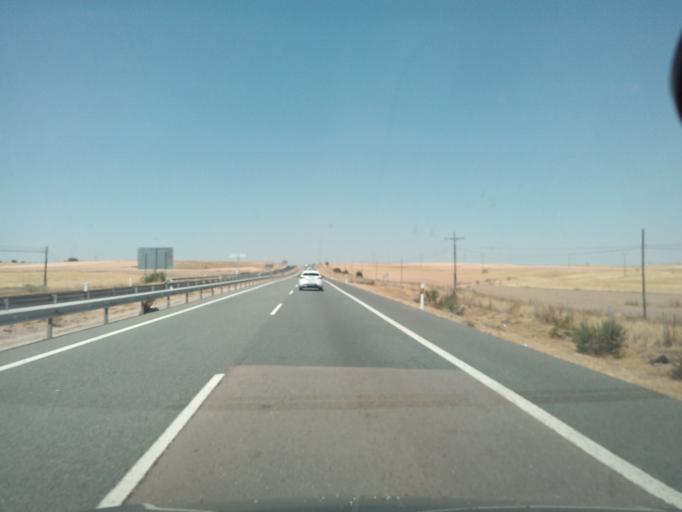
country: ES
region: Castille-La Mancha
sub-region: Province of Toledo
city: Tembleque
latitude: 39.7045
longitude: -3.4976
